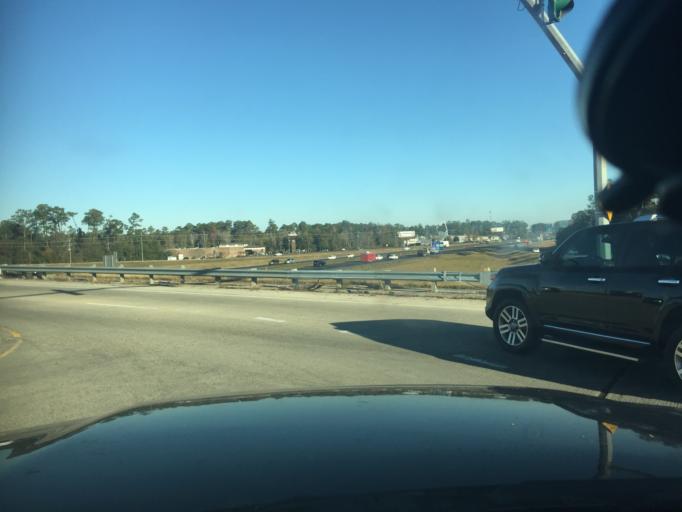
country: US
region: Louisiana
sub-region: Saint Tammany Parish
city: Slidell
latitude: 30.2699
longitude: -89.7541
